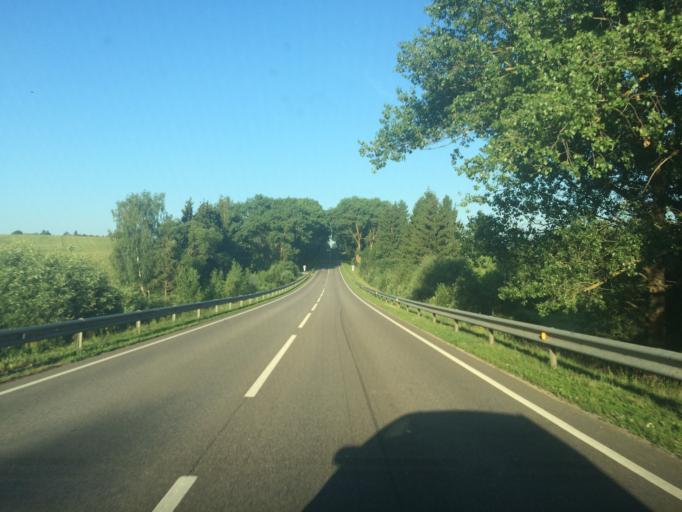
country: LT
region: Utenos apskritis
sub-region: Anyksciai
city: Anyksciai
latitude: 55.3981
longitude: 25.0869
